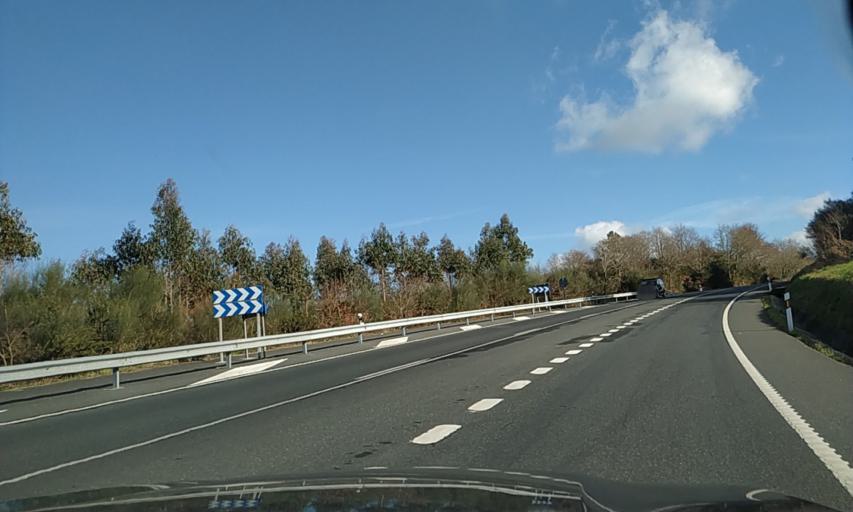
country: ES
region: Galicia
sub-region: Provincia de Pontevedra
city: Silleda
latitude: 42.7087
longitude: -8.3482
